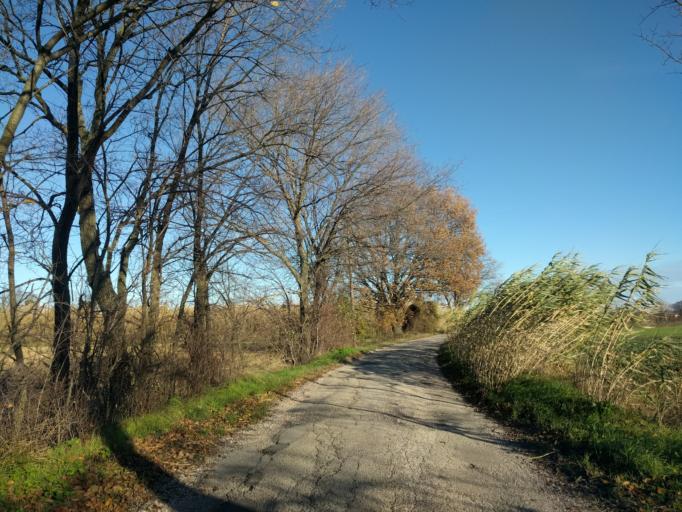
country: IT
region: The Marches
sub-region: Provincia di Pesaro e Urbino
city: Cuccurano
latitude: 43.7972
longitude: 12.9786
